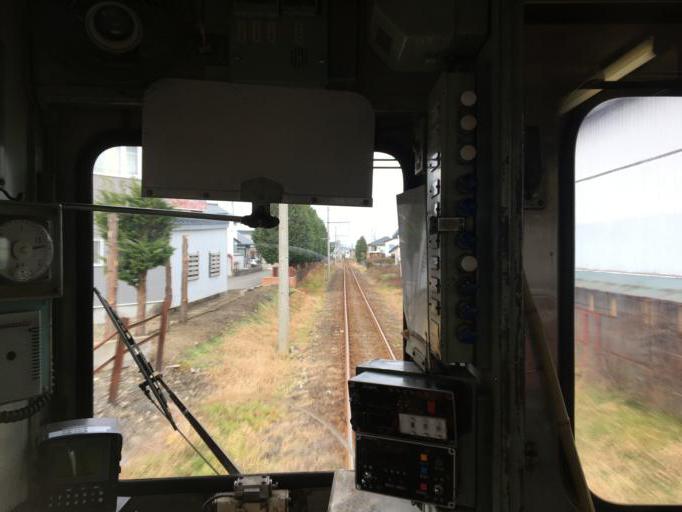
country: JP
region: Aomori
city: Hirosaki
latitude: 40.5714
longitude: 140.4760
